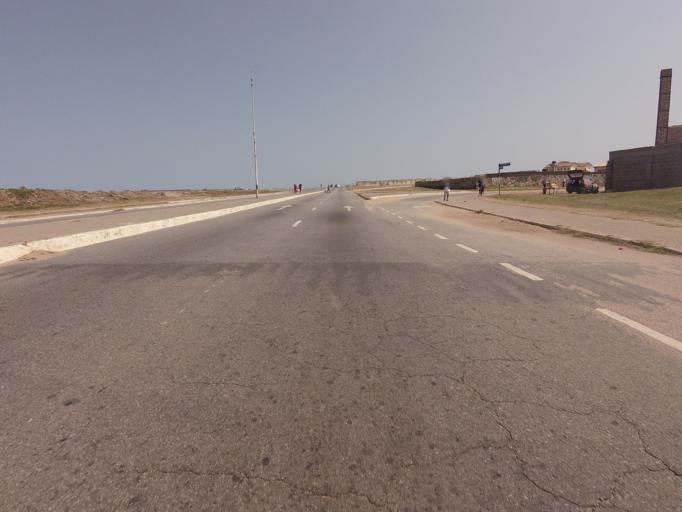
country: GH
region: Greater Accra
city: Accra
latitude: 5.5321
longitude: -0.2220
